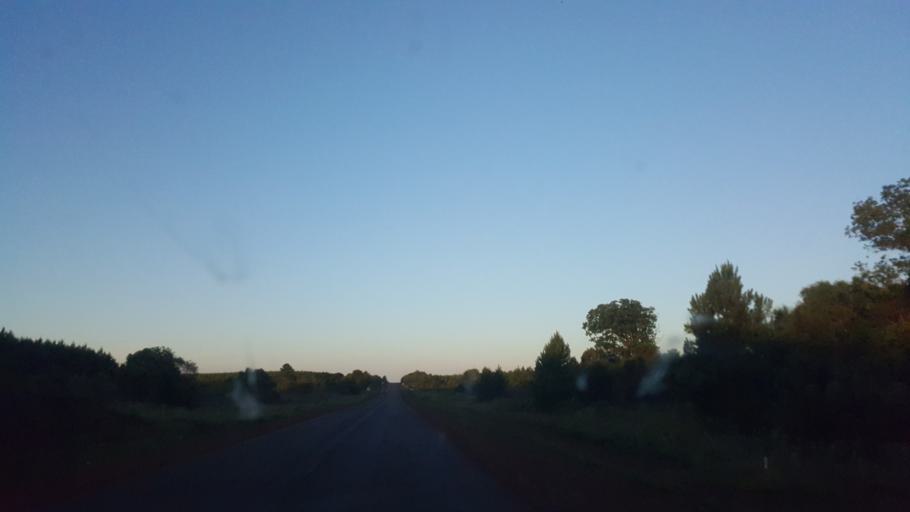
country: AR
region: Corrientes
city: Santo Tome
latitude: -28.4111
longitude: -55.9825
